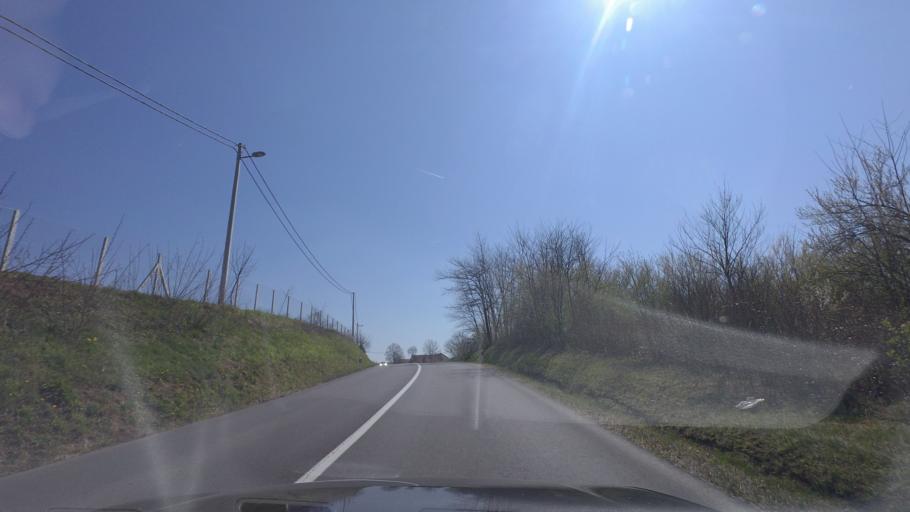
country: HR
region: Karlovacka
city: Vojnic
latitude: 45.3439
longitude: 15.6846
